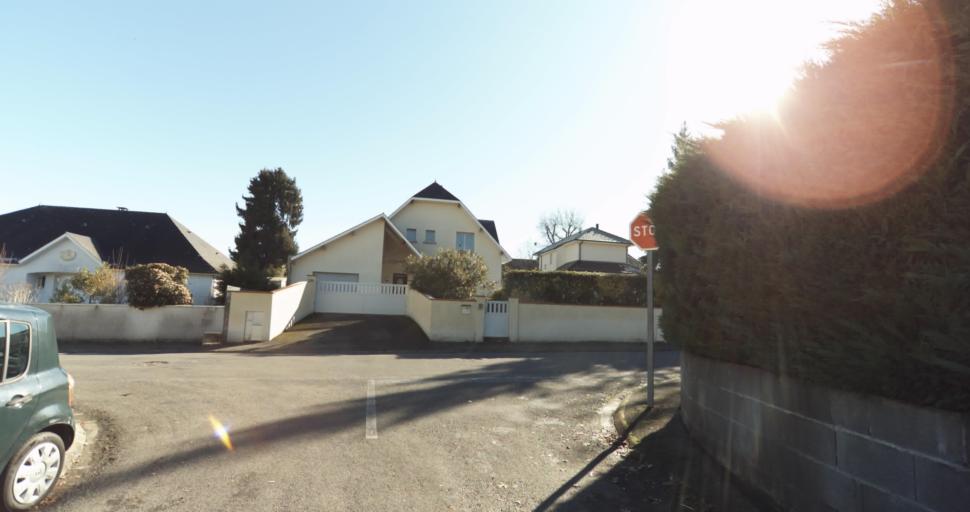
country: FR
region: Aquitaine
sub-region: Departement des Pyrenees-Atlantiques
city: Morlaas
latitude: 43.3433
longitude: -0.2678
